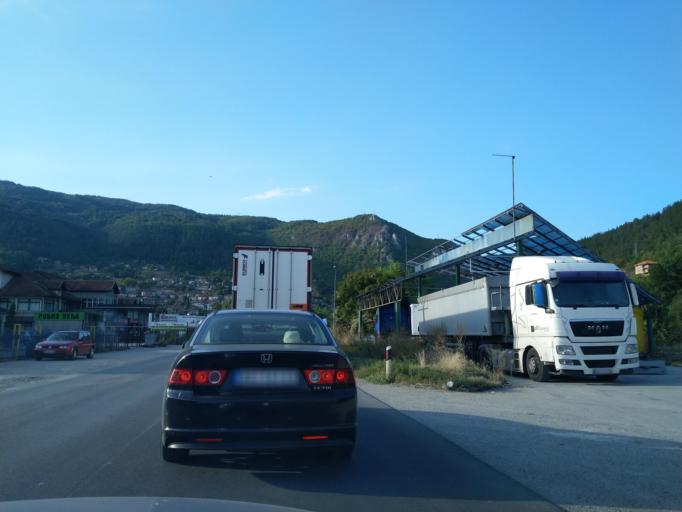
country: RS
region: Central Serbia
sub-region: Zlatiborski Okrug
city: Prijepolje
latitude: 43.3691
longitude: 19.6329
